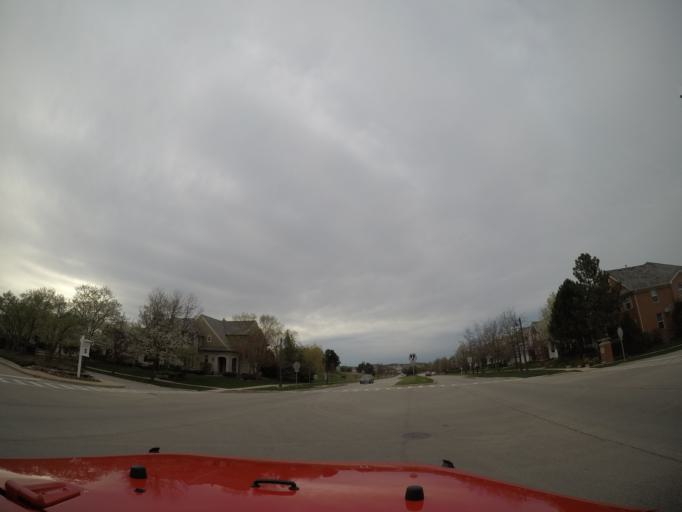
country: US
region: Illinois
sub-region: Cook County
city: Glenview
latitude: 42.0816
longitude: -87.8196
